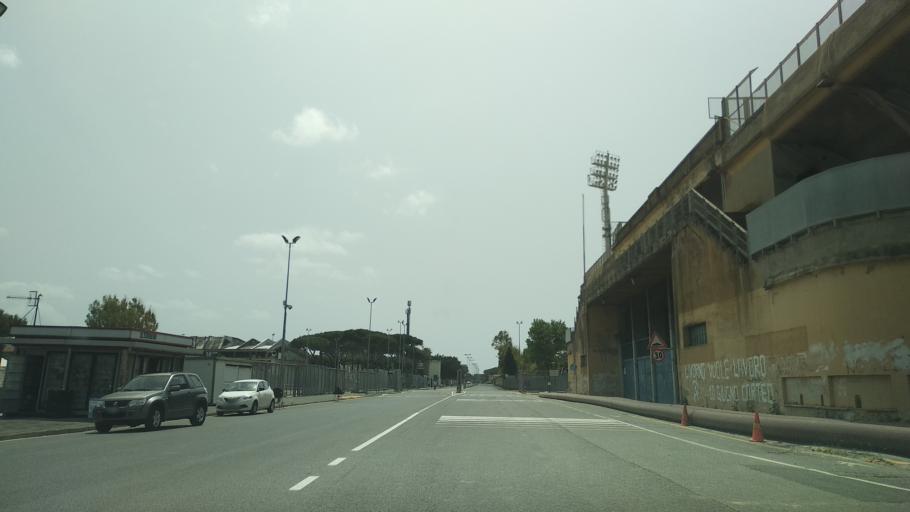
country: IT
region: Tuscany
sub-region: Provincia di Livorno
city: Livorno
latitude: 43.5273
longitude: 10.3153
